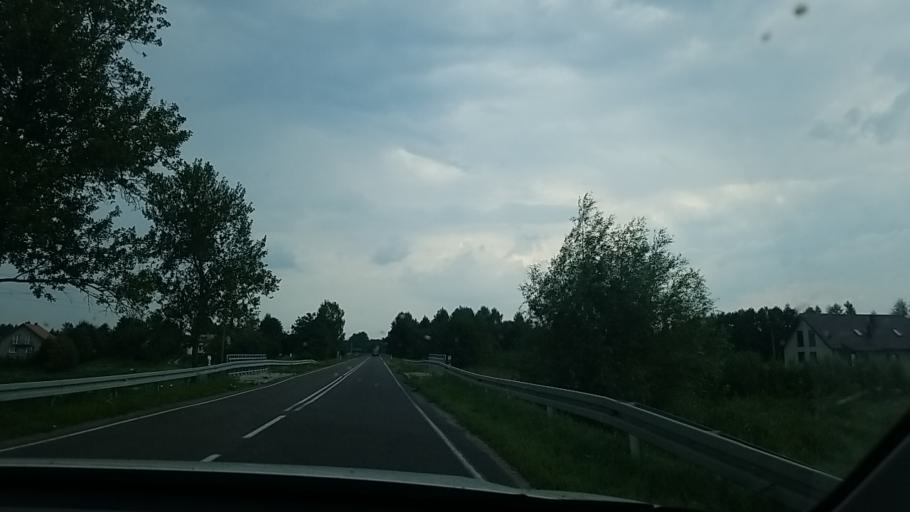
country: PL
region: Lublin Voivodeship
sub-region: Powiat leczynski
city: Cycow
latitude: 51.2371
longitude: 23.0863
